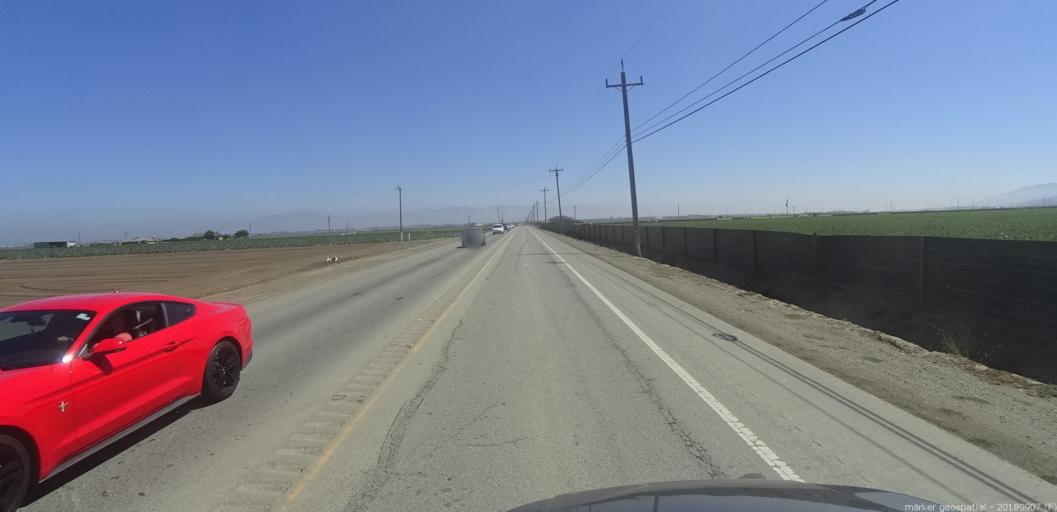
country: US
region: California
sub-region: Monterey County
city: Boronda
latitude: 36.6787
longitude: -121.7293
